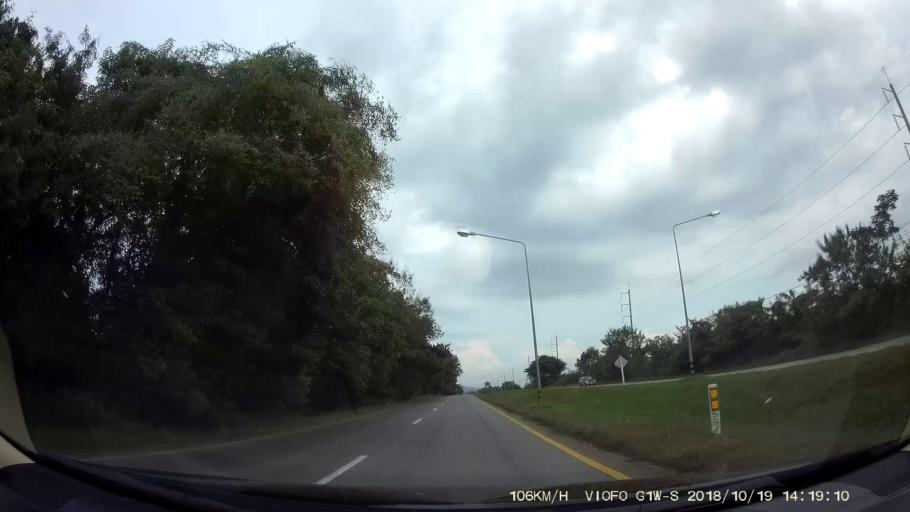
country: TH
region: Chaiyaphum
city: Kaeng Khro
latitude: 16.0247
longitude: 102.2428
